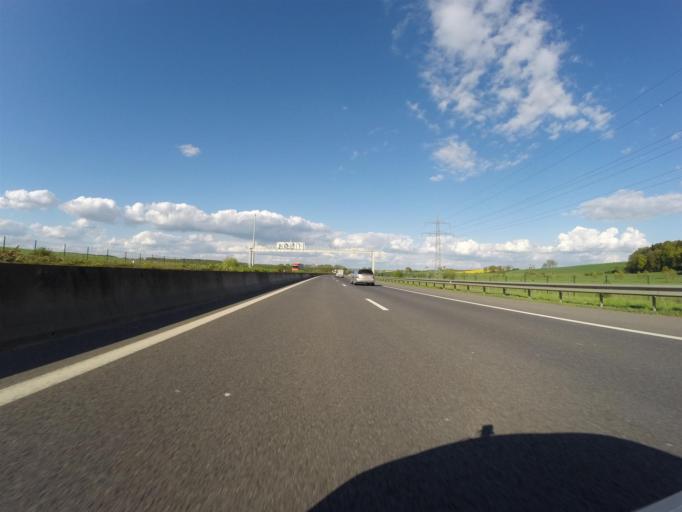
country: LU
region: Luxembourg
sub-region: Canton d'Esch-sur-Alzette
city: Frisange
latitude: 49.5071
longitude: 6.1618
